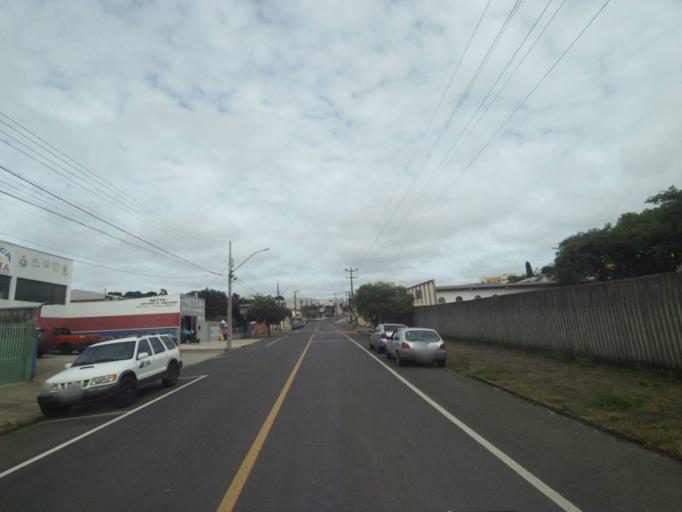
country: BR
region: Parana
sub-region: Telemaco Borba
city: Telemaco Borba
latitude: -24.3346
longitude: -50.6223
